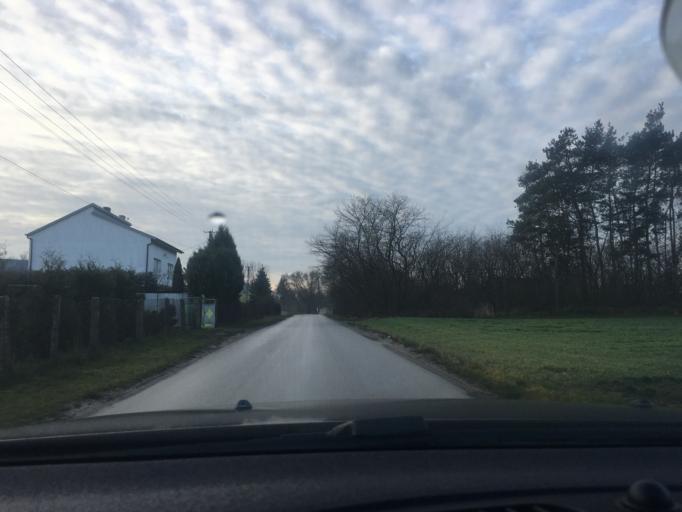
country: PL
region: Swietokrzyskie
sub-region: Powiat jedrzejowski
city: Imielno
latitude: 50.6330
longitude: 20.4092
